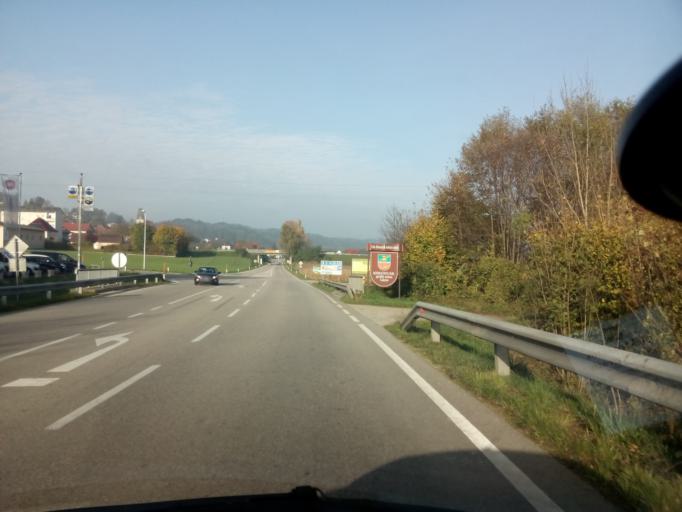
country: AT
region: Upper Austria
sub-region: Politischer Bezirk Steyr-Land
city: Bad Hall
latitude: 48.1043
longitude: 14.1906
